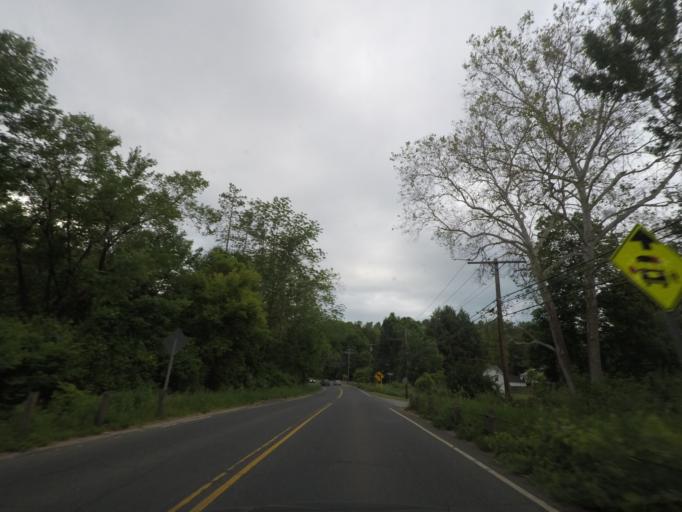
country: US
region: Connecticut
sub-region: Litchfield County
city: Canaan
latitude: 41.9373
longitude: -73.3942
